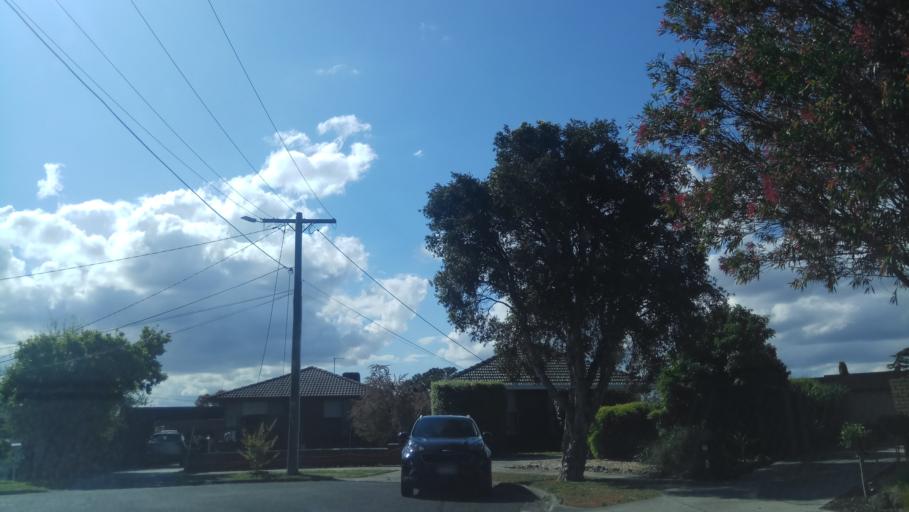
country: AU
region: Victoria
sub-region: Kingston
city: Dingley Village
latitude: -37.9786
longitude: 145.1231
